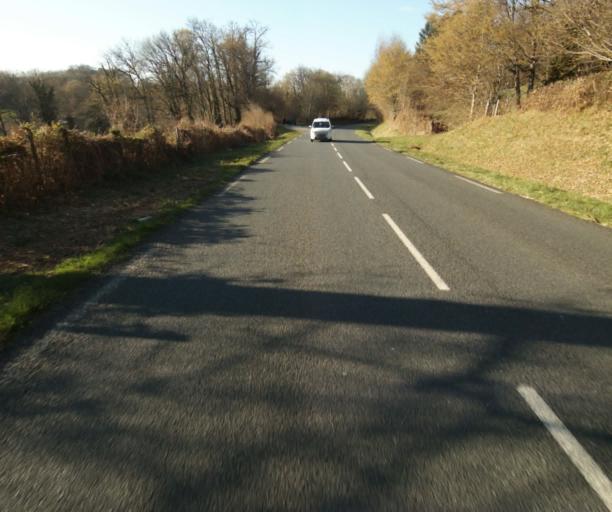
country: FR
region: Limousin
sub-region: Departement de la Correze
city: Seilhac
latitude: 45.3933
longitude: 1.7179
